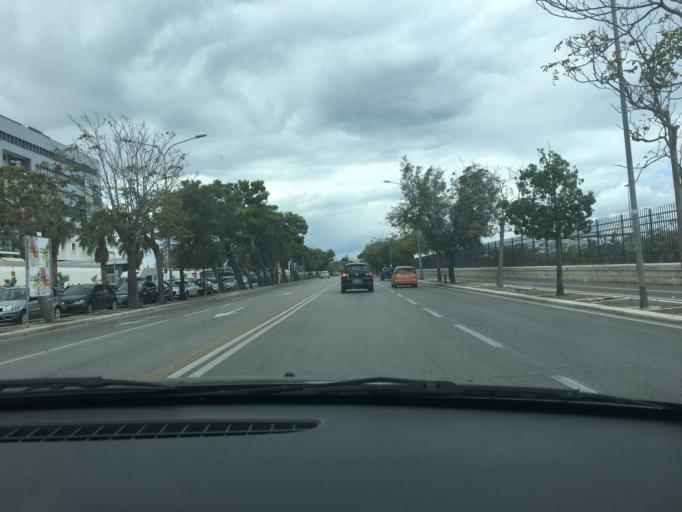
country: IT
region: Apulia
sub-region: Provincia di Bari
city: Bari
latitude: 41.1297
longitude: 16.8511
